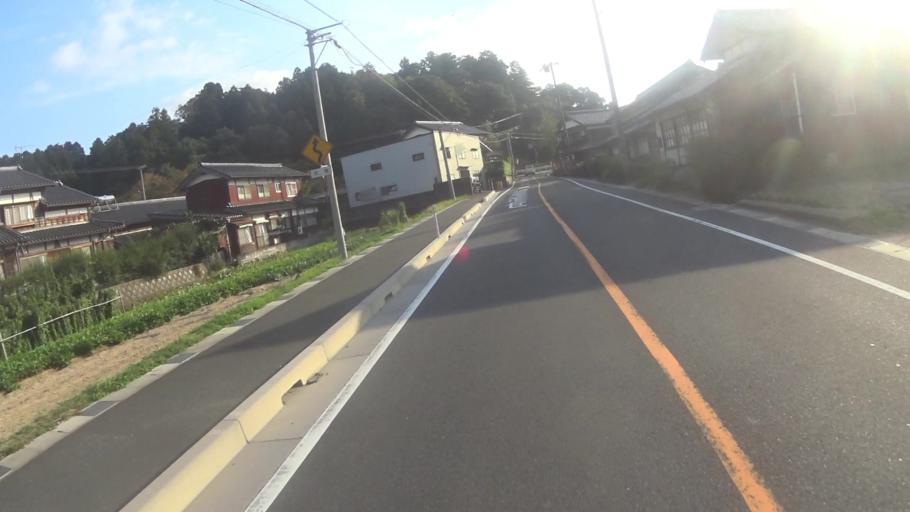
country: JP
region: Kyoto
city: Miyazu
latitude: 35.6776
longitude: 135.0982
